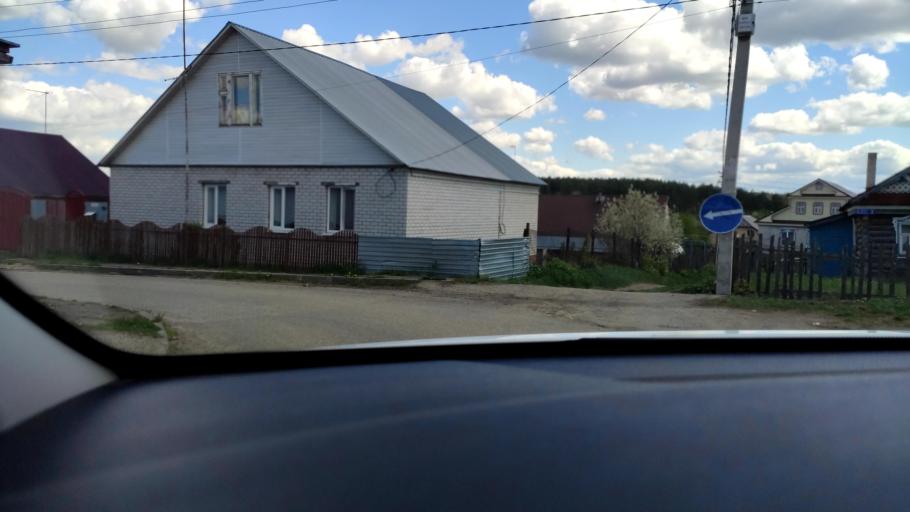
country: RU
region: Tatarstan
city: Stolbishchi
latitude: 55.7023
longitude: 49.1534
